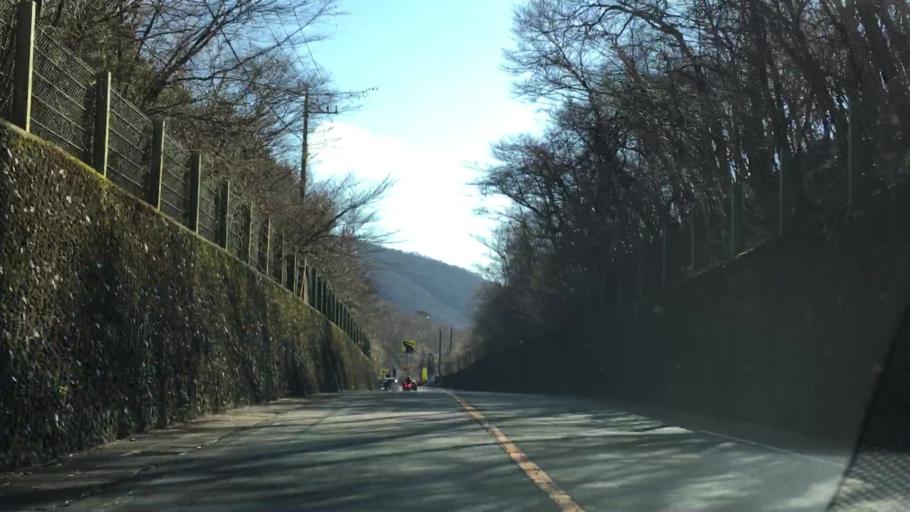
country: JP
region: Shizuoka
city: Gotemba
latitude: 35.3931
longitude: 138.8640
